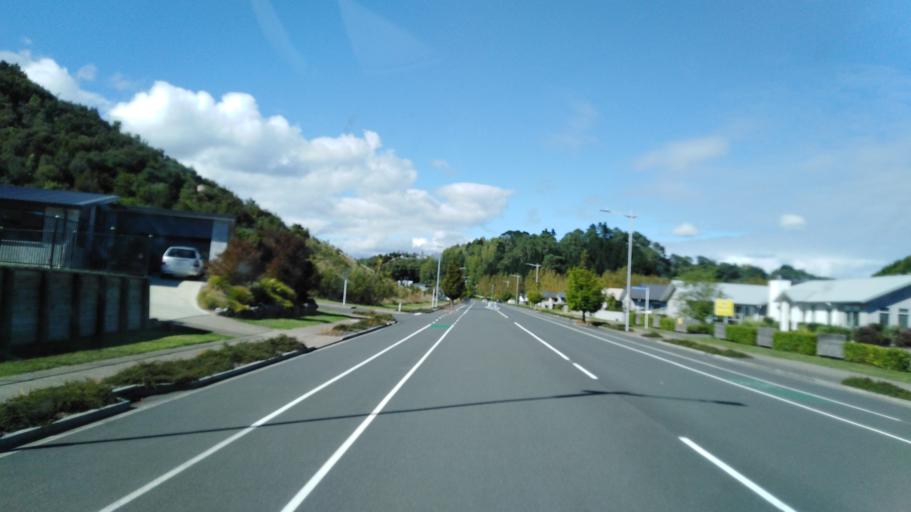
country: NZ
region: Bay of Plenty
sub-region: Tauranga City
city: Tauranga
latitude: -37.7566
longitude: 176.1039
